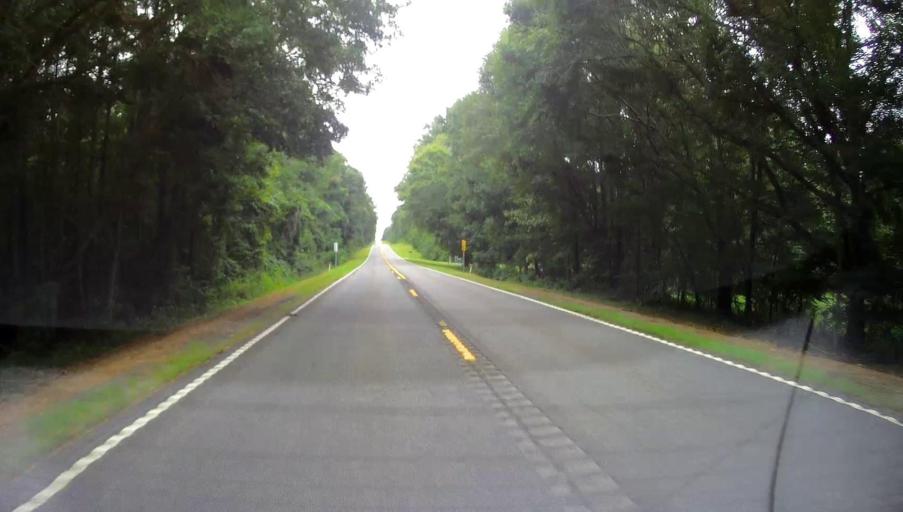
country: US
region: Georgia
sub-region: Dooly County
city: Unadilla
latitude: 32.2913
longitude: -83.8658
